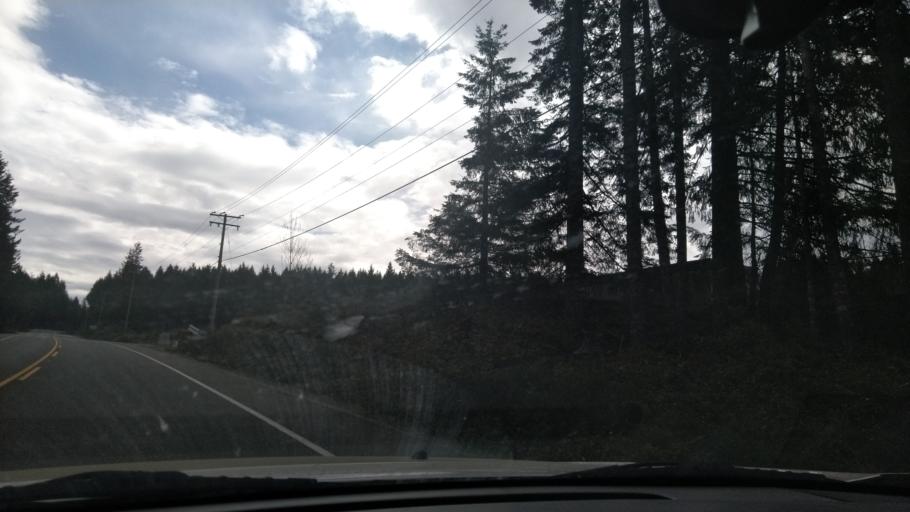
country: CA
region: British Columbia
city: Campbell River
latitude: 50.0239
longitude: -125.3534
